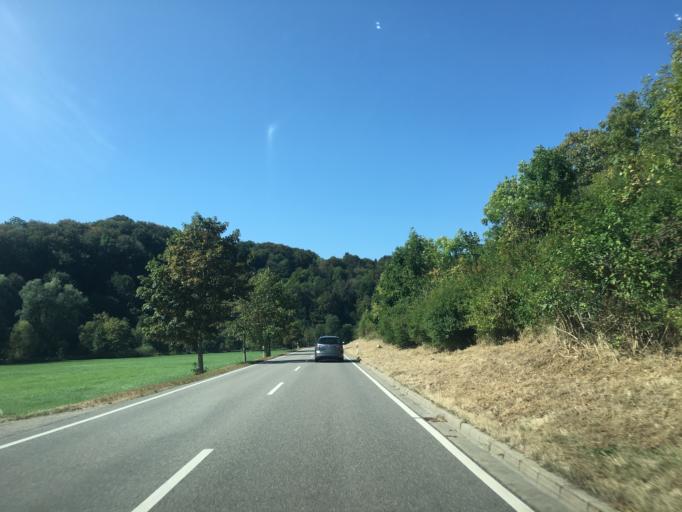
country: DE
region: Baden-Wuerttemberg
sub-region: Tuebingen Region
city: Munsingen
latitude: 48.3461
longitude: 9.4847
